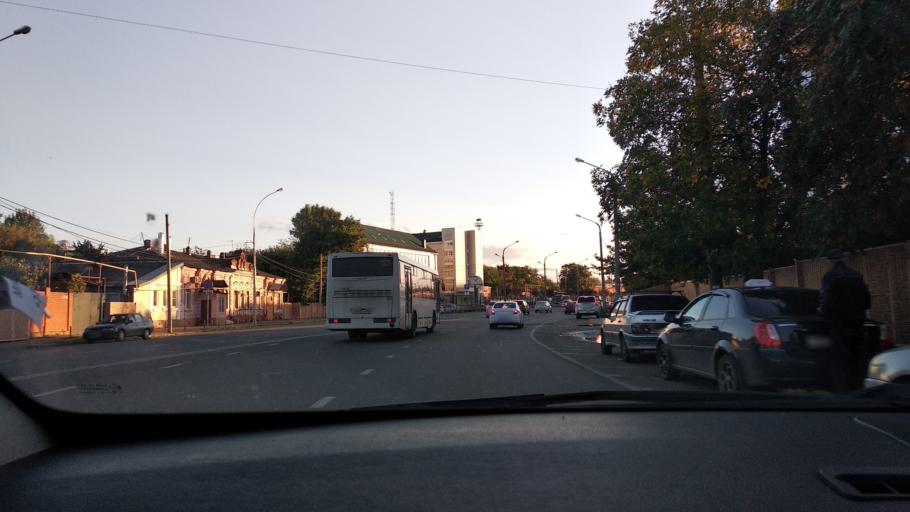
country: RU
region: Krasnodarskiy
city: Krasnodar
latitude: 45.0169
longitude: 38.9801
